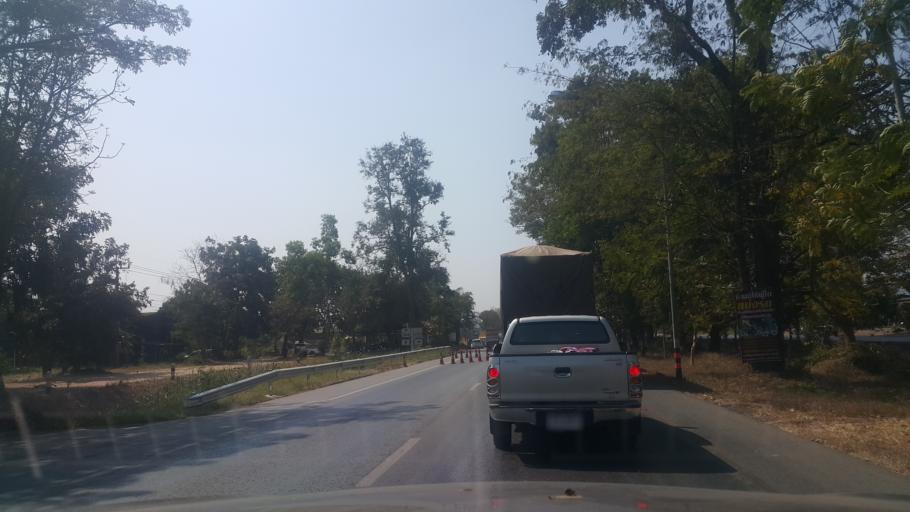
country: TH
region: Nakhon Ratchasima
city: Pak Thong Chai
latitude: 14.5606
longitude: 101.9766
